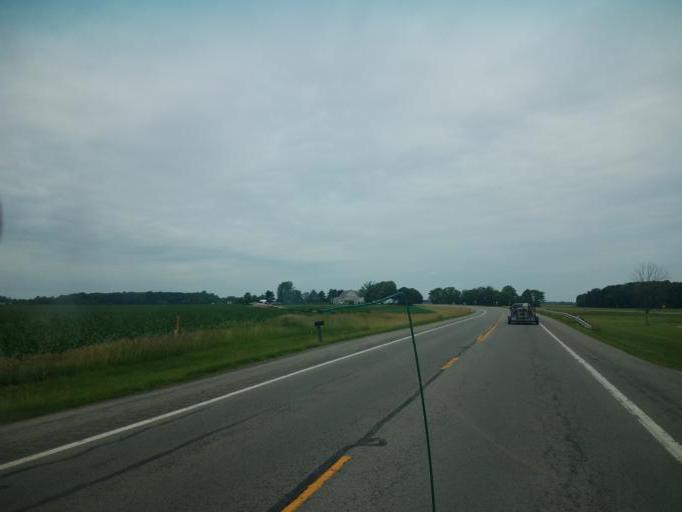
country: US
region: Ohio
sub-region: Hardin County
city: Ada
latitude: 40.7315
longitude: -83.7950
